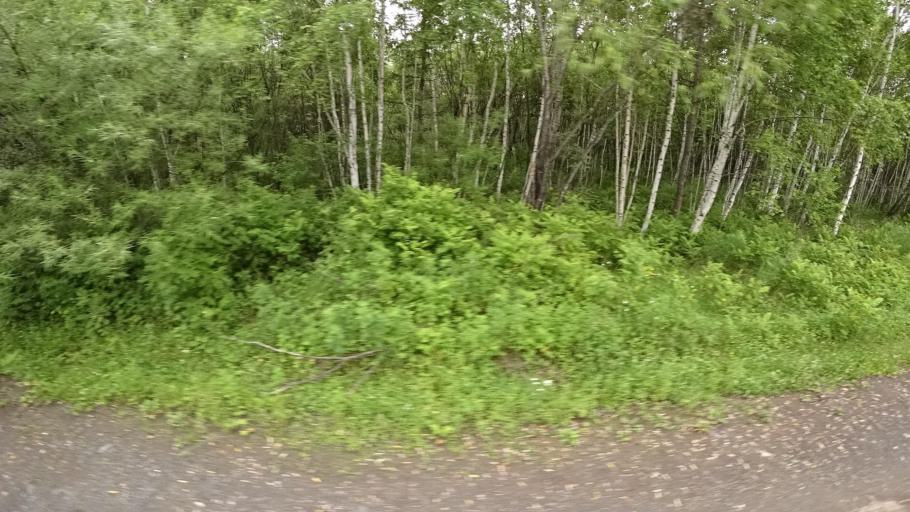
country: RU
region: Khabarovsk Krai
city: Amursk
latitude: 49.9131
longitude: 136.1587
